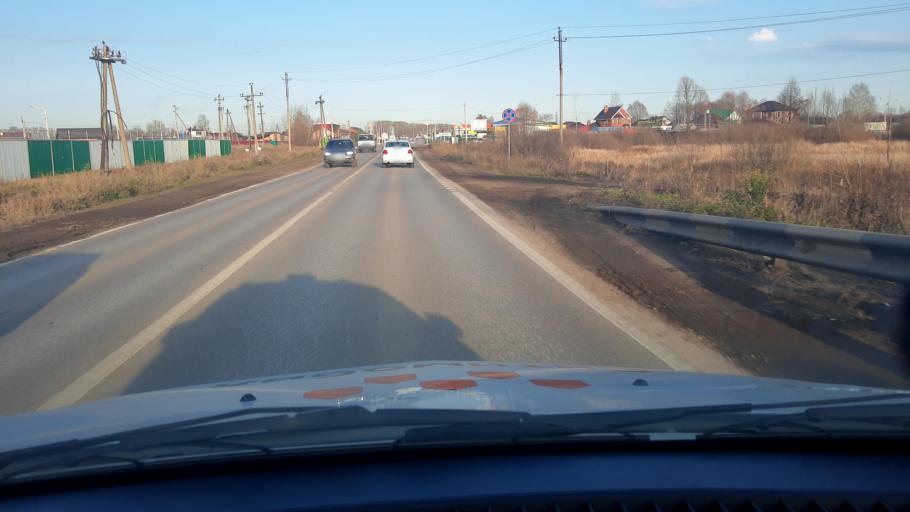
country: RU
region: Bashkortostan
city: Ufa
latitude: 54.6722
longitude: 56.0846
